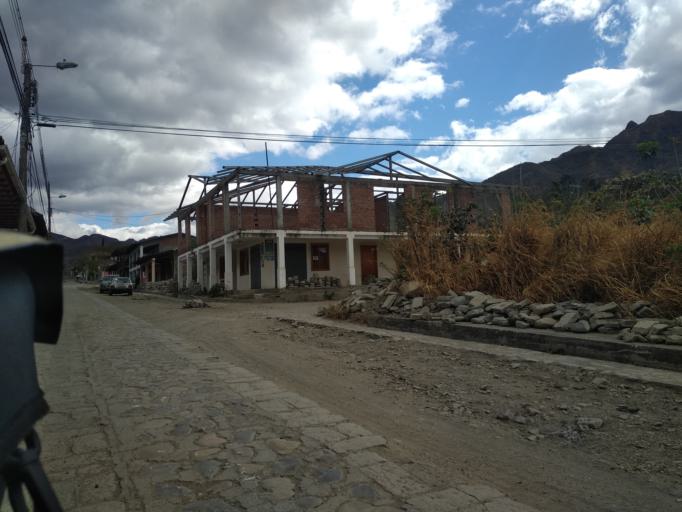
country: EC
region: Loja
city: Loja
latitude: -4.2581
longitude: -79.2218
